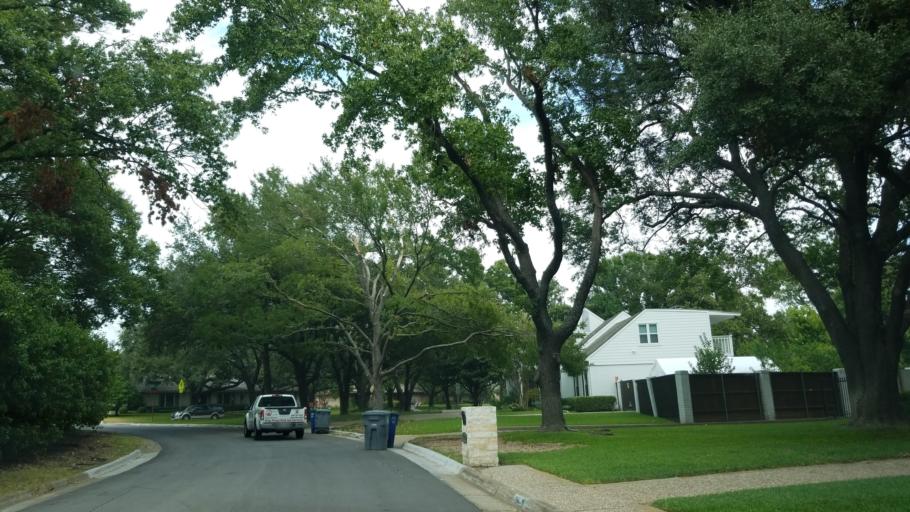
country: US
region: Texas
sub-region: Dallas County
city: Richardson
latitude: 32.9444
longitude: -96.7798
